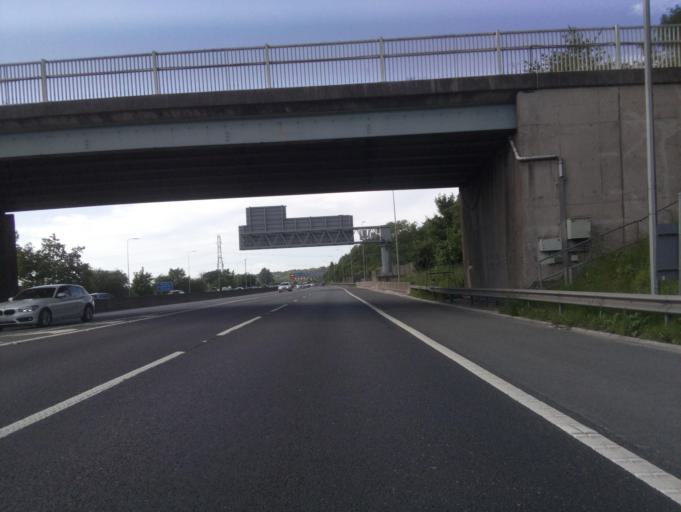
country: GB
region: England
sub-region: Manchester
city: Swinton
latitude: 53.4908
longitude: -2.3787
